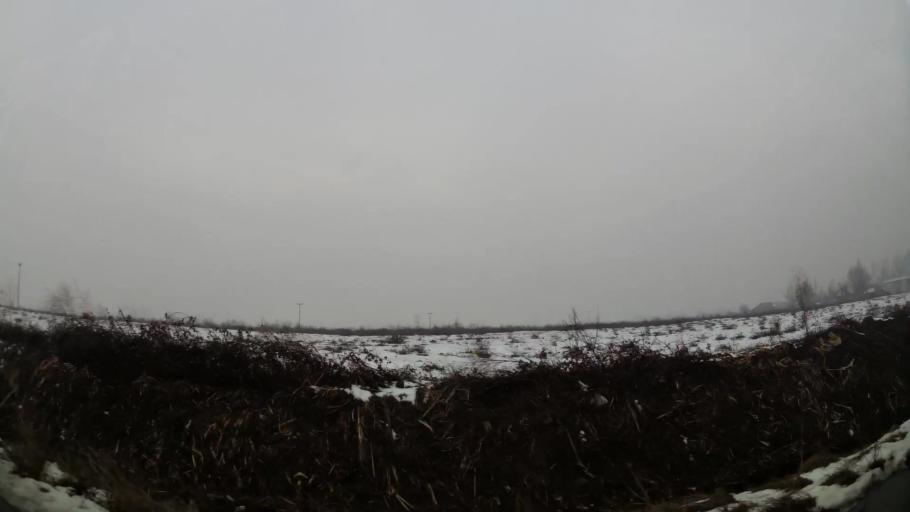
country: MK
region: Petrovec
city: Petrovec
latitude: 41.9340
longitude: 21.6079
